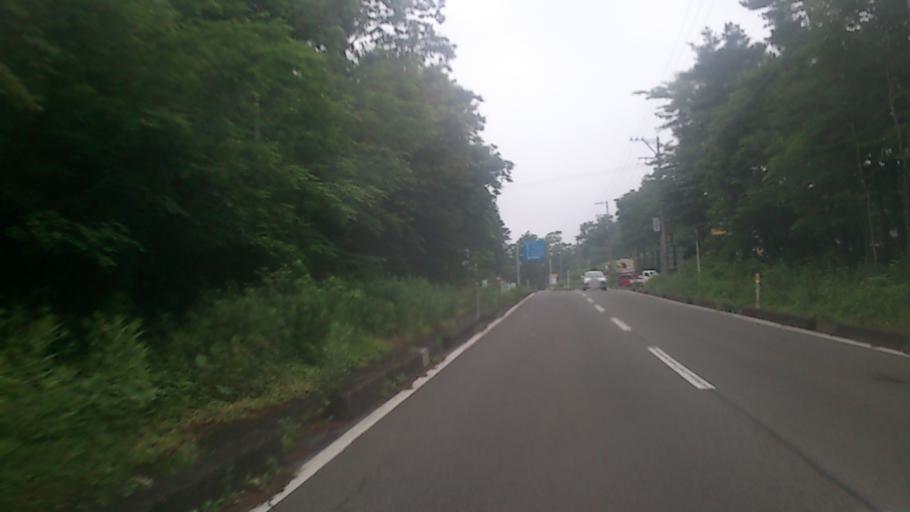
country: JP
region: Miyagi
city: Shiroishi
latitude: 38.1141
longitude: 140.5669
